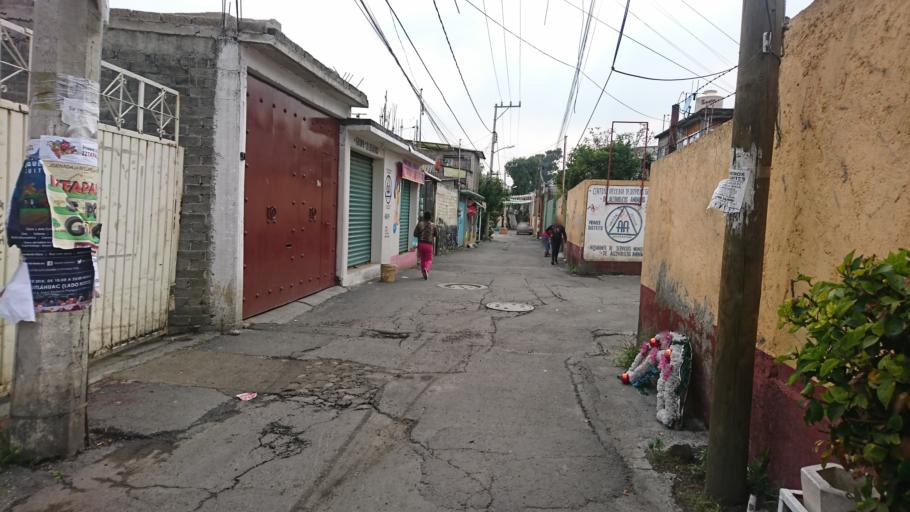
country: MX
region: Mexico City
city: Iztapalapa
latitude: 19.3266
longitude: -99.1033
